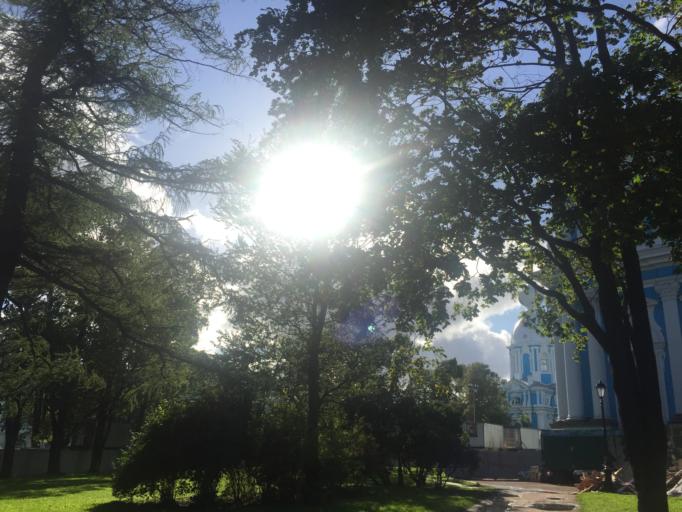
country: RU
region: Leningrad
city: Finlyandskiy
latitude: 59.9488
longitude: 30.3968
